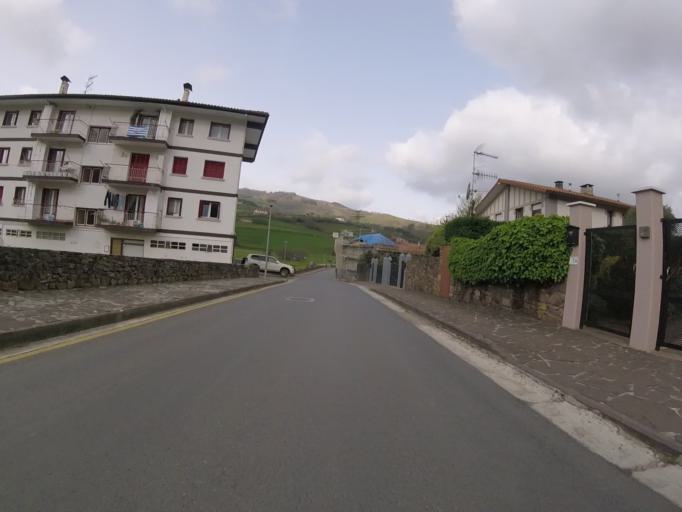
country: ES
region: Basque Country
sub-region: Provincia de Guipuzcoa
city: Berastegui
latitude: 43.1230
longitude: -1.9808
